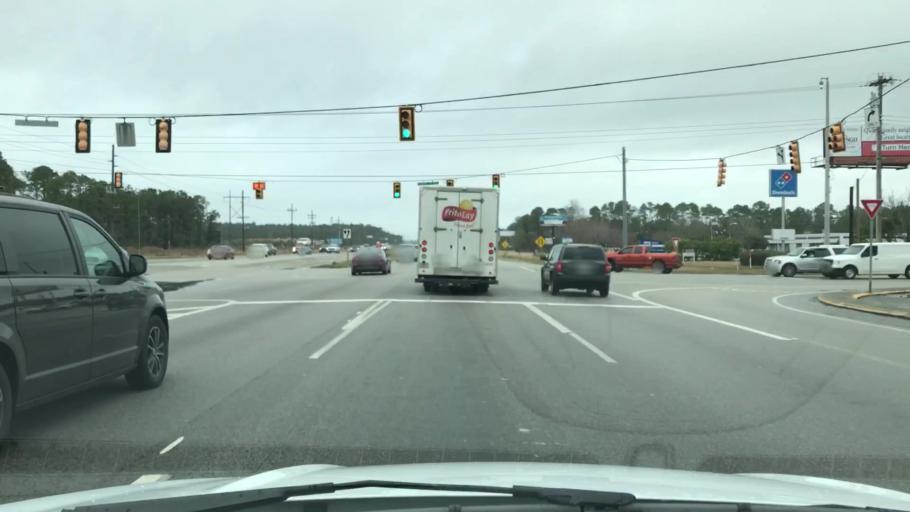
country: US
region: South Carolina
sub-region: Horry County
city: Red Hill
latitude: 33.7753
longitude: -78.9828
